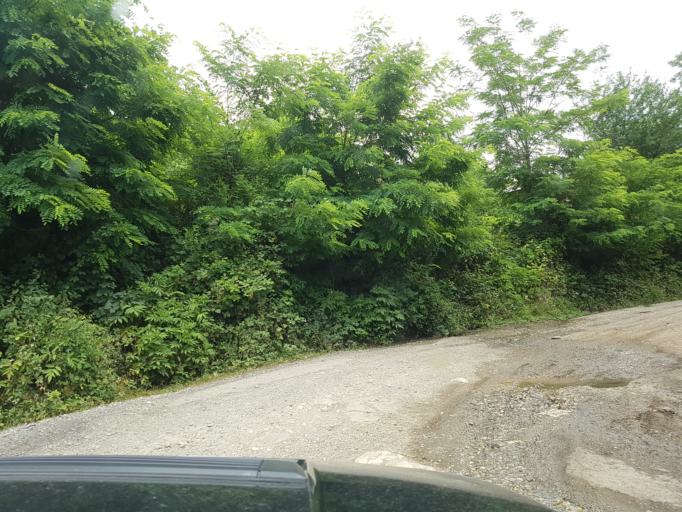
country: GE
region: Imereti
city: Tsqaltubo
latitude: 42.4774
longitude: 42.7533
